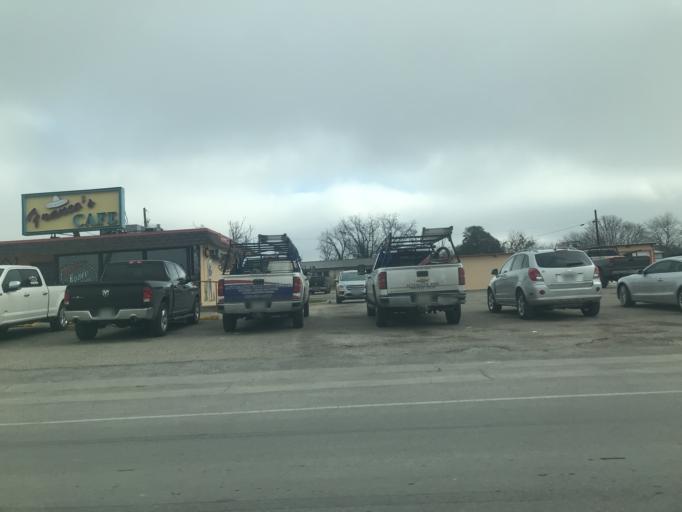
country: US
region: Texas
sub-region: Tom Green County
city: San Angelo
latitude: 31.4813
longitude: -100.4540
